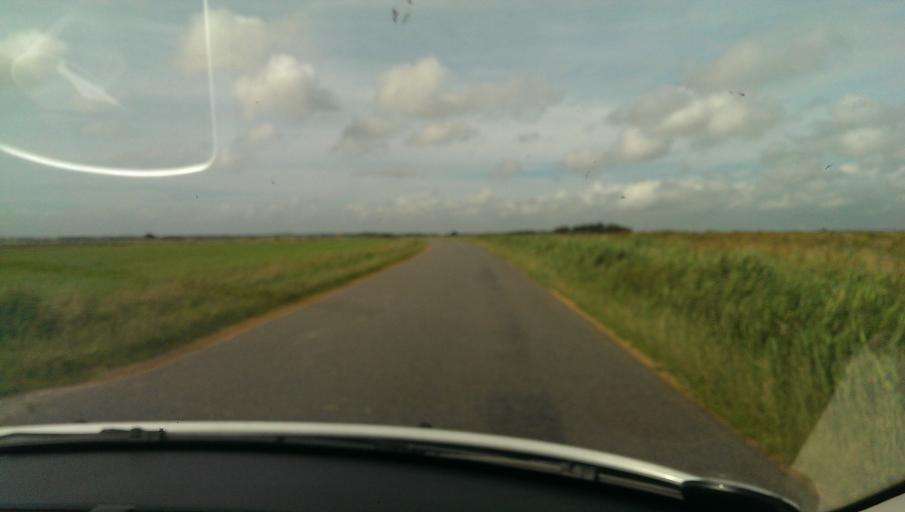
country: DK
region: Central Jutland
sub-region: Holstebro Kommune
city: Ulfborg
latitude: 56.2841
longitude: 8.2345
